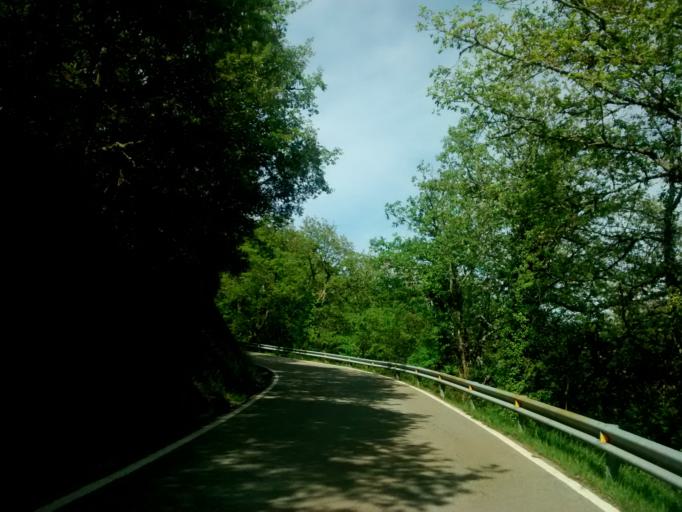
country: ES
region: Cantabria
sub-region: Provincia de Cantabria
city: Potes
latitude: 43.1923
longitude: -4.6275
